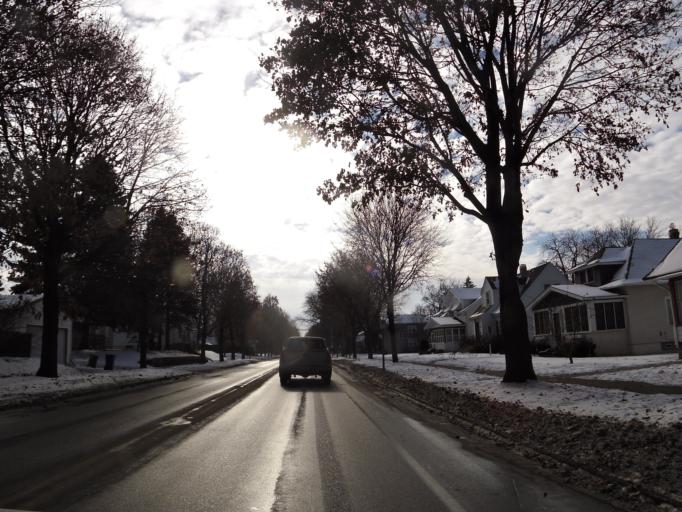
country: US
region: Minnesota
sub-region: Ramsey County
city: Falcon Heights
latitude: 44.9334
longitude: -93.1874
